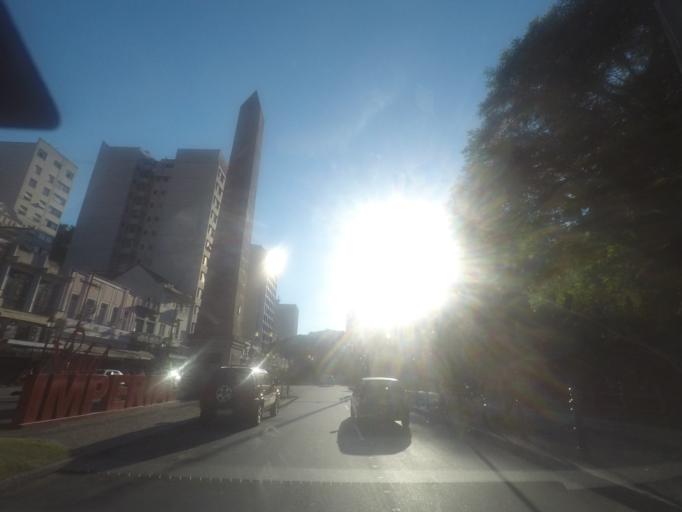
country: BR
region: Rio de Janeiro
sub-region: Petropolis
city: Petropolis
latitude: -22.5099
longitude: -43.1752
